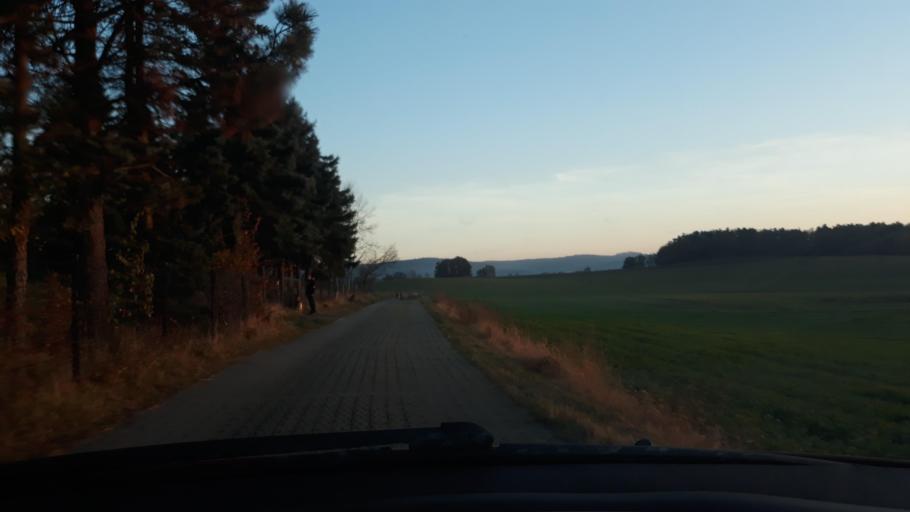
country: DE
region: Saxony
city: Kirchberg
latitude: 50.6134
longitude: 12.5309
